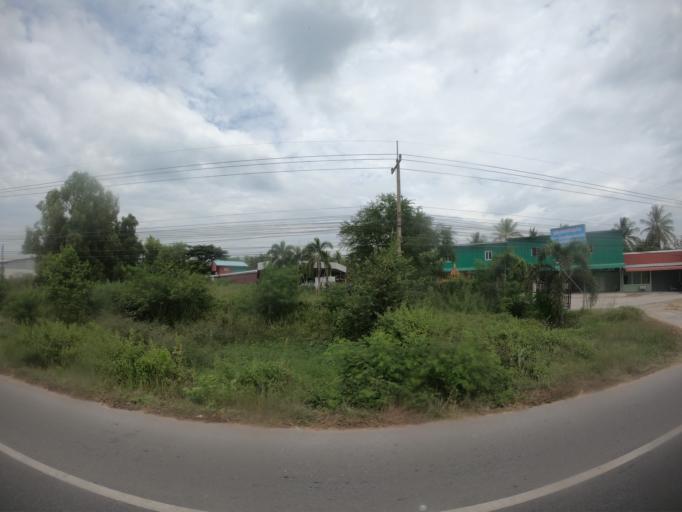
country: TH
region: Maha Sarakham
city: Maha Sarakham
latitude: 16.1575
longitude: 103.3670
